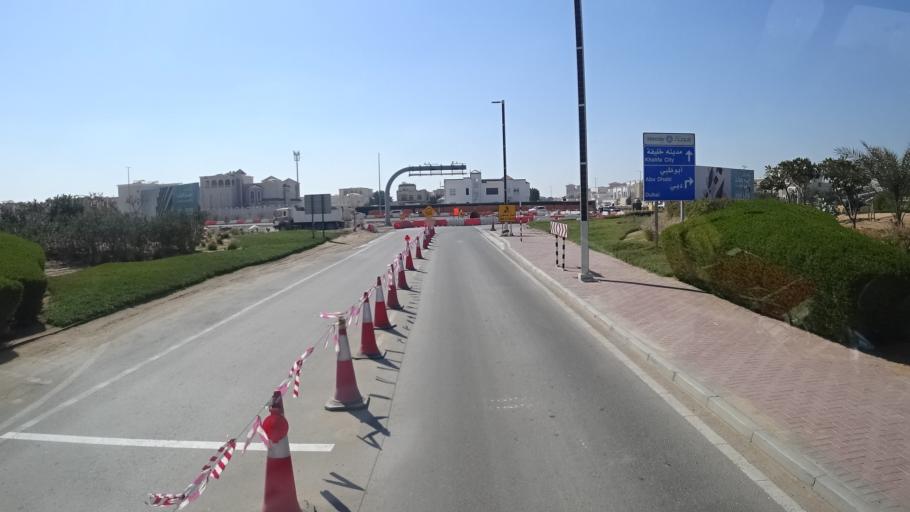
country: AE
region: Abu Dhabi
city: Abu Dhabi
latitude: 24.4316
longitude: 54.6056
